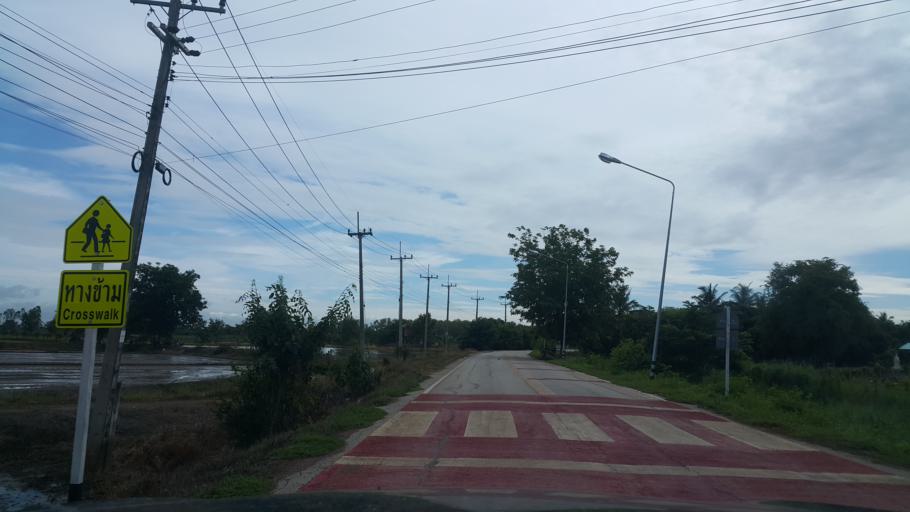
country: TH
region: Sukhothai
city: Si Nakhon
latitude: 17.2768
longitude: 99.9926
